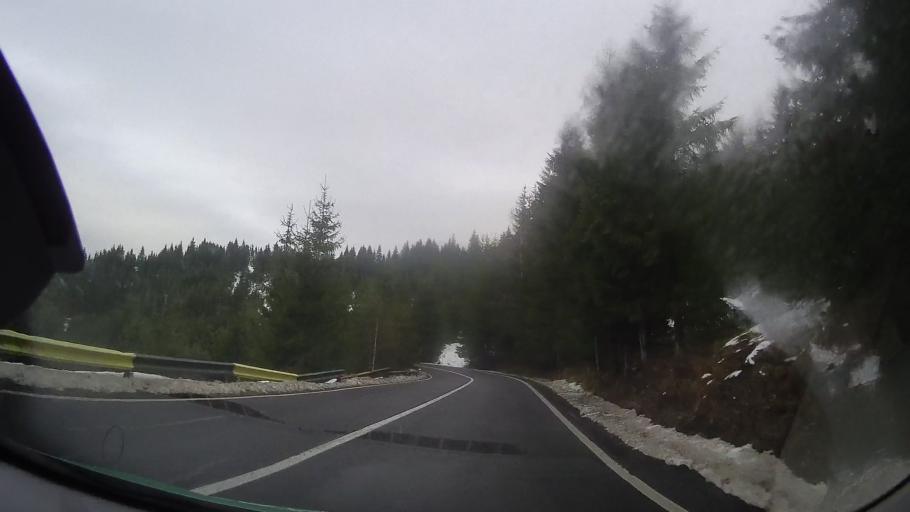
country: RO
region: Harghita
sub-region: Municipiul Gheorgheni
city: Gheorgheni
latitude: 46.7766
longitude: 25.7124
